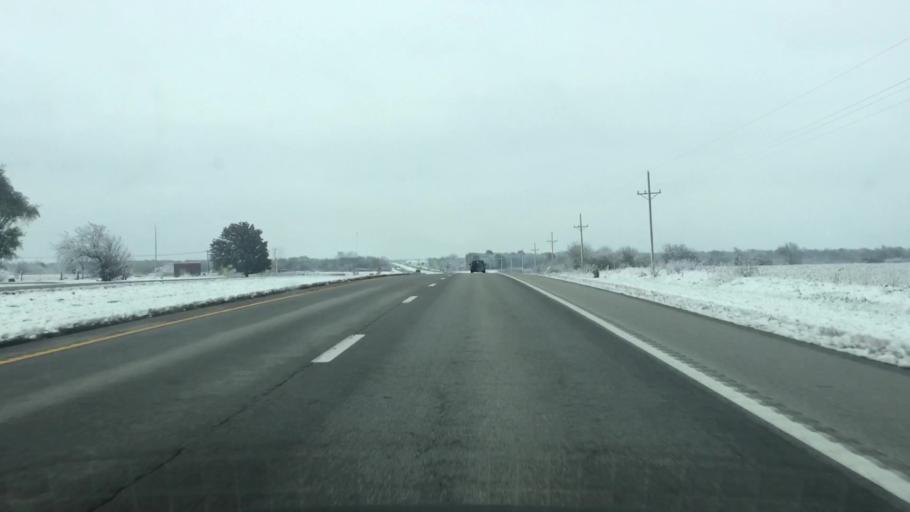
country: US
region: Missouri
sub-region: Cass County
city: Garden City
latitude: 38.5852
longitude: -94.2276
